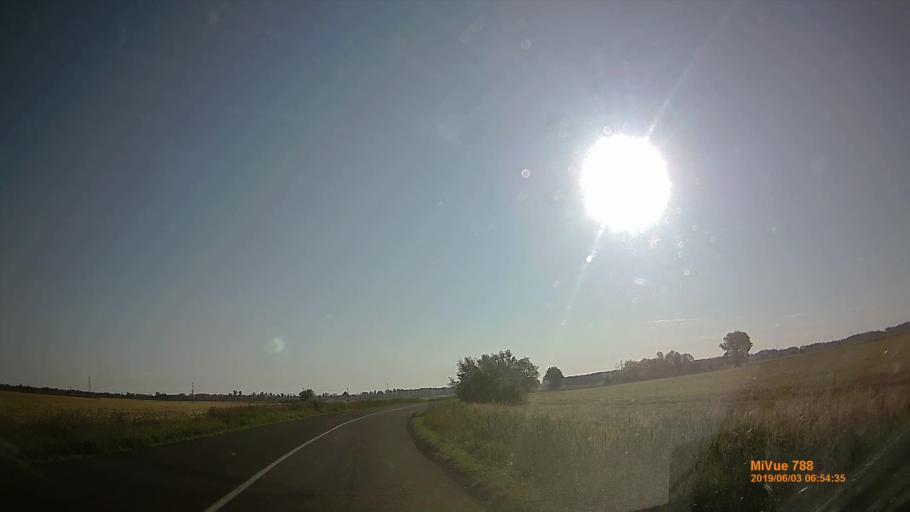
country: HU
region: Pest
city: Bugyi
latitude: 47.2160
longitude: 19.2279
